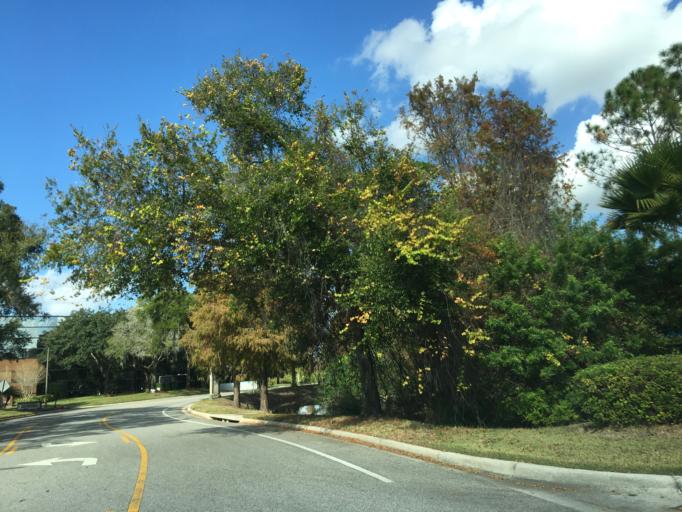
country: US
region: Florida
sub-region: Orange County
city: Eatonville
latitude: 28.6231
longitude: -81.3903
